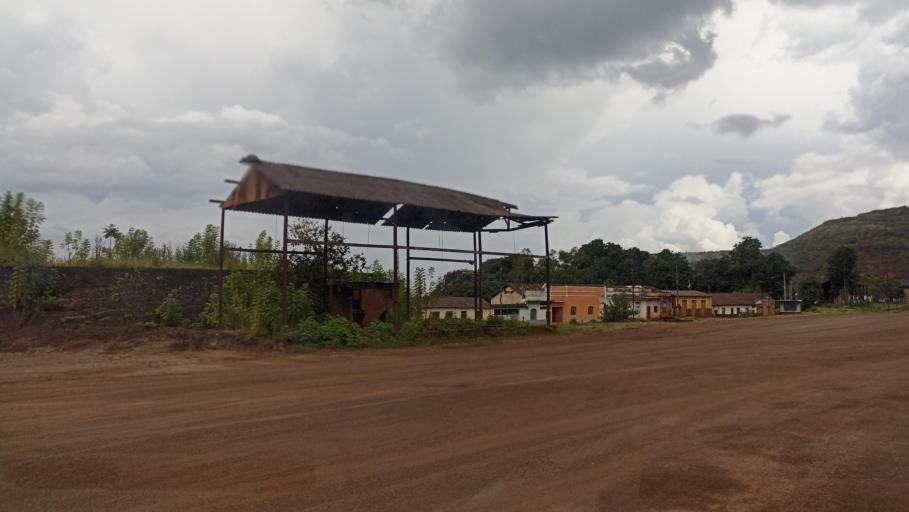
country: BR
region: Minas Gerais
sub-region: Congonhas
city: Congonhas
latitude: -20.4343
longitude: -43.7728
